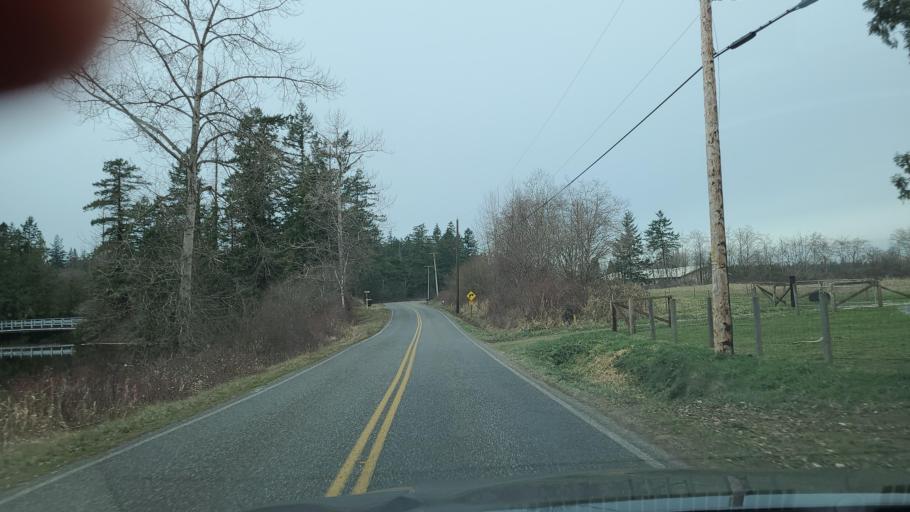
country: US
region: Washington
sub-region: Whatcom County
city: Birch Bay
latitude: 48.9503
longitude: -122.7095
